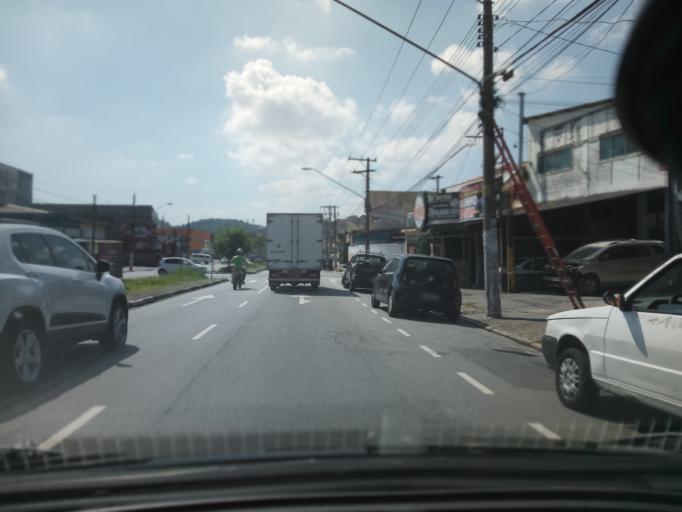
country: BR
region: Sao Paulo
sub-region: Sao Bernardo Do Campo
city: Sao Bernardo do Campo
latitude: -23.7148
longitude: -46.5325
